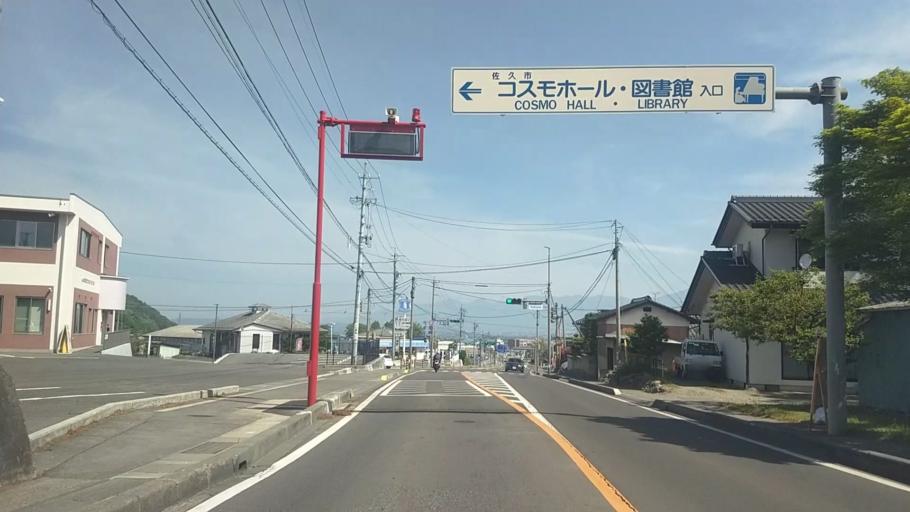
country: JP
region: Nagano
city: Saku
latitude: 36.1881
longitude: 138.4808
